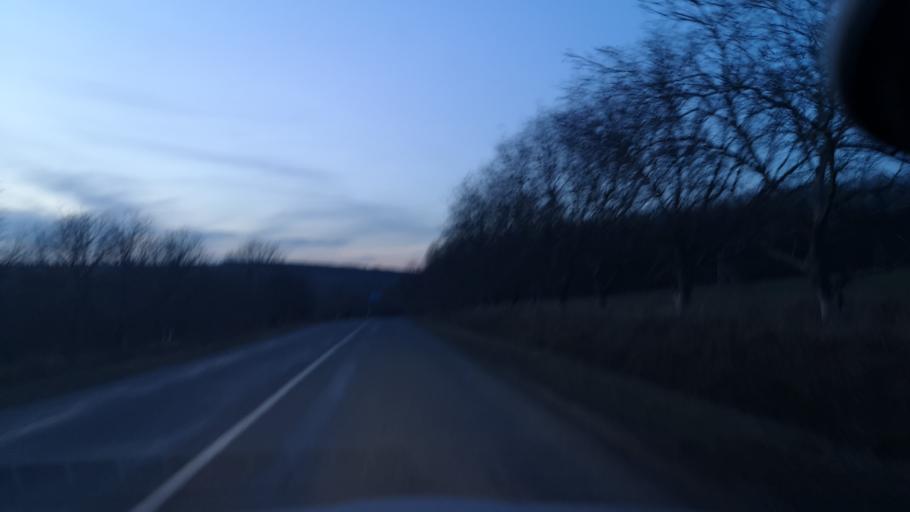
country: MD
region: Orhei
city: Orhei
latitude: 47.2913
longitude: 28.8124
